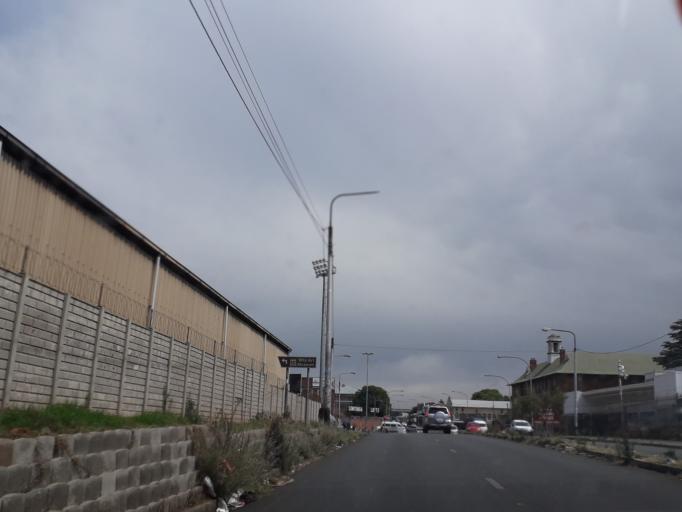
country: ZA
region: Gauteng
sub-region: City of Johannesburg Metropolitan Municipality
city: Johannesburg
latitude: -26.1927
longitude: 28.0204
